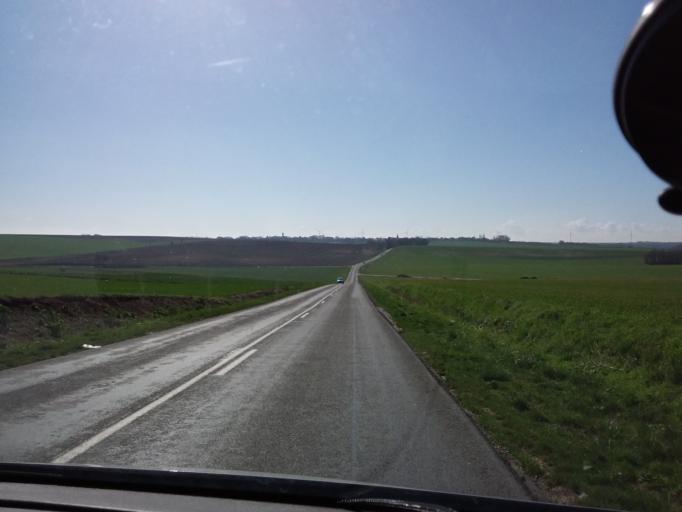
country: FR
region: Picardie
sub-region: Departement de l'Aisne
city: Montcornet
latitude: 49.6499
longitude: 4.0207
